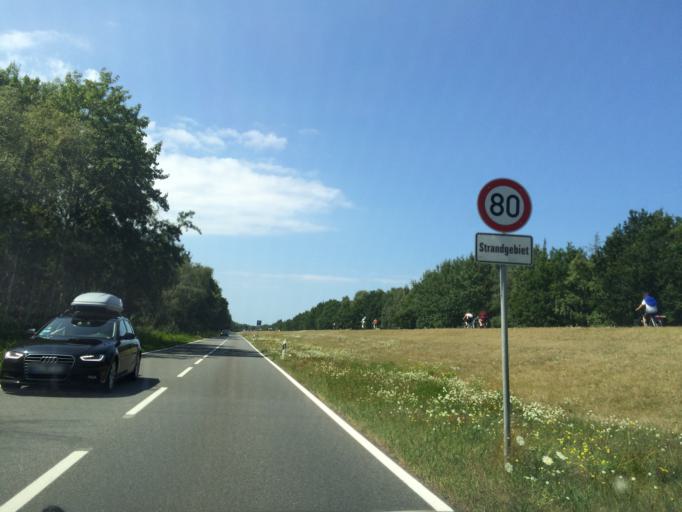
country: DE
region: Mecklenburg-Vorpommern
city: Zingst
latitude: 54.4418
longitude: 12.6588
